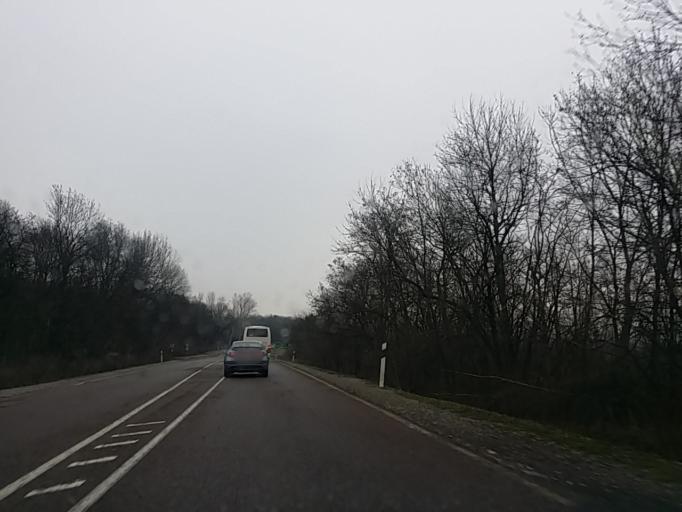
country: HU
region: Borsod-Abauj-Zemplen
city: Mezokovesd
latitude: 47.8387
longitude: 20.6384
